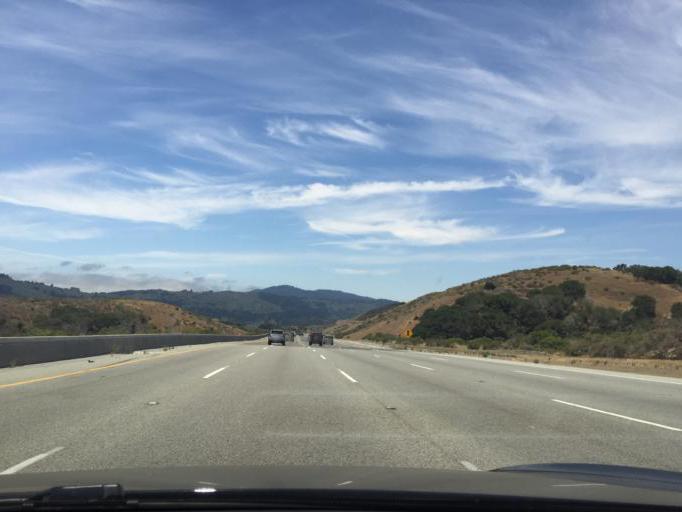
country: US
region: California
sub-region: San Mateo County
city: Belmont
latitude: 37.4949
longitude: -122.3058
